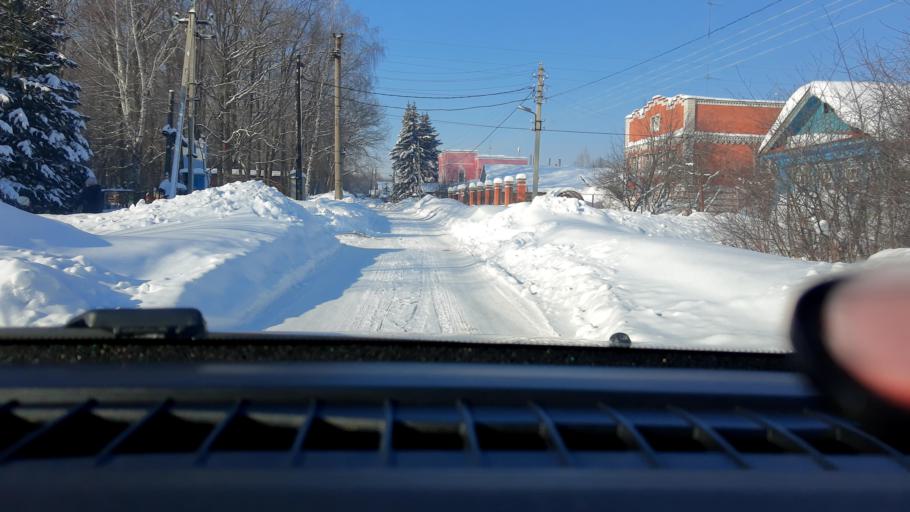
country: RU
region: Nizjnij Novgorod
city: Afonino
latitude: 56.1989
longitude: 44.0346
